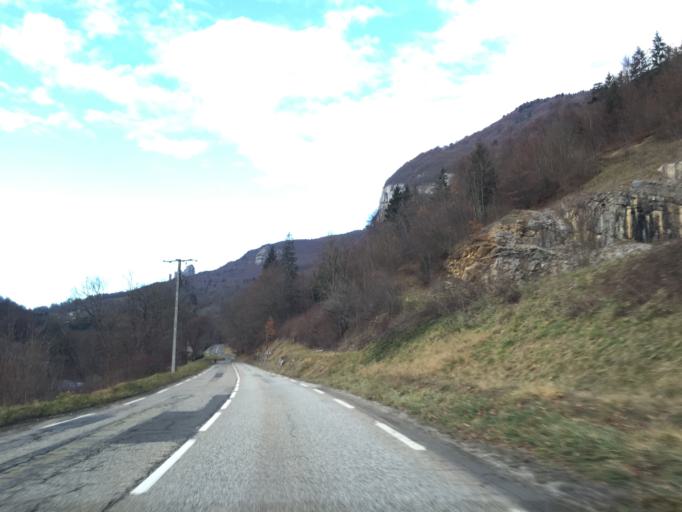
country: FR
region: Rhone-Alpes
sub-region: Departement de la Haute-Savoie
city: Gruffy
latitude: 45.7425
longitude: 6.0978
